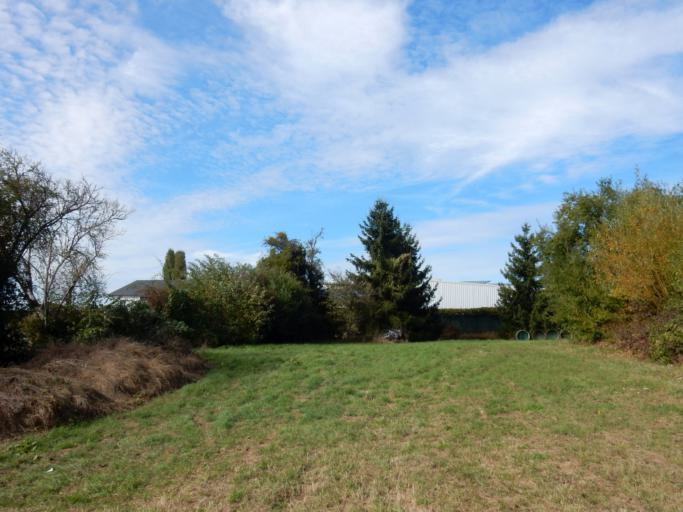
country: LU
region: Grevenmacher
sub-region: Canton de Grevenmacher
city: Wormeldange
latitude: 49.6131
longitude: 6.3983
